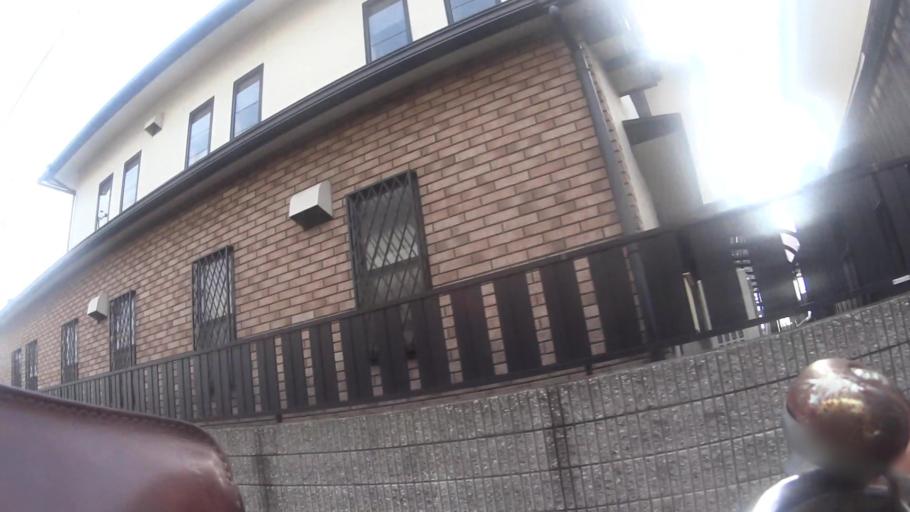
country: JP
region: Kyoto
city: Muko
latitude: 34.9416
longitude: 135.7065
